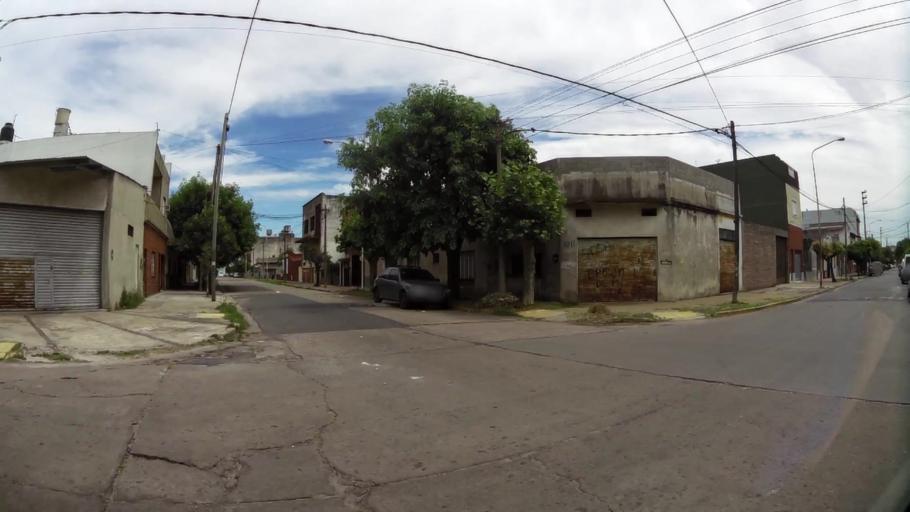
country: AR
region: Buenos Aires
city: San Justo
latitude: -34.6705
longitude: -58.5457
